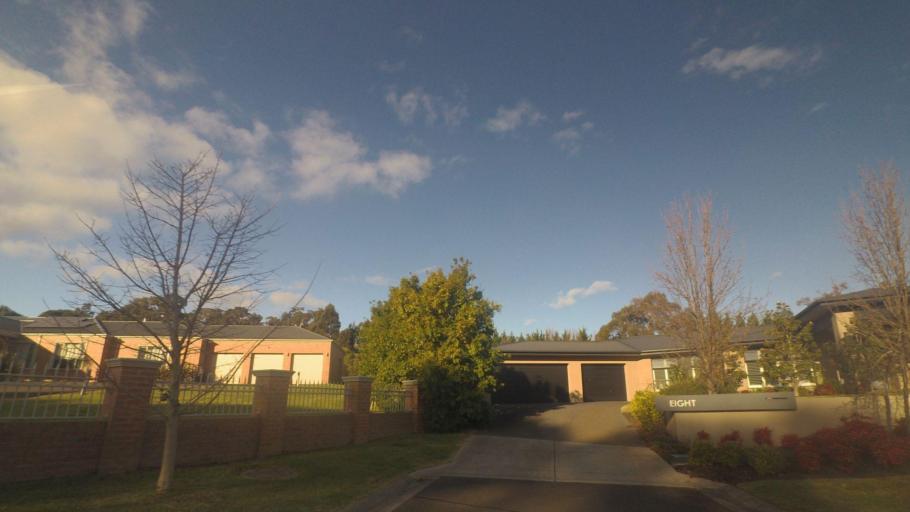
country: AU
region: Victoria
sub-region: Yarra Ranges
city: Lysterfield
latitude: -37.9146
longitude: 145.2929
